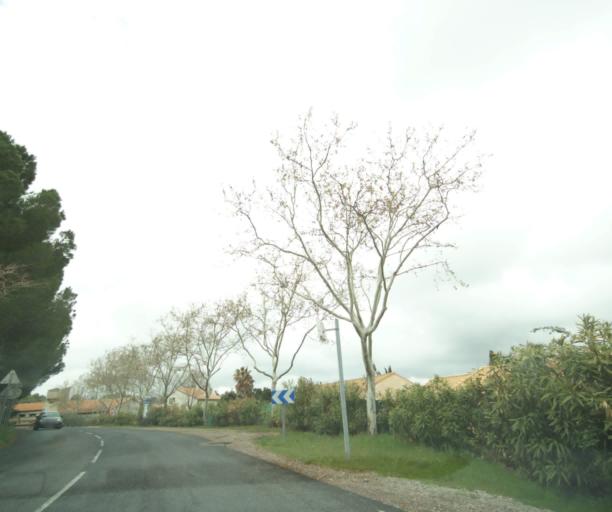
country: FR
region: Languedoc-Roussillon
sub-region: Departement de l'Herault
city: Murviel-les-Montpellier
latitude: 43.6033
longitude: 3.7396
